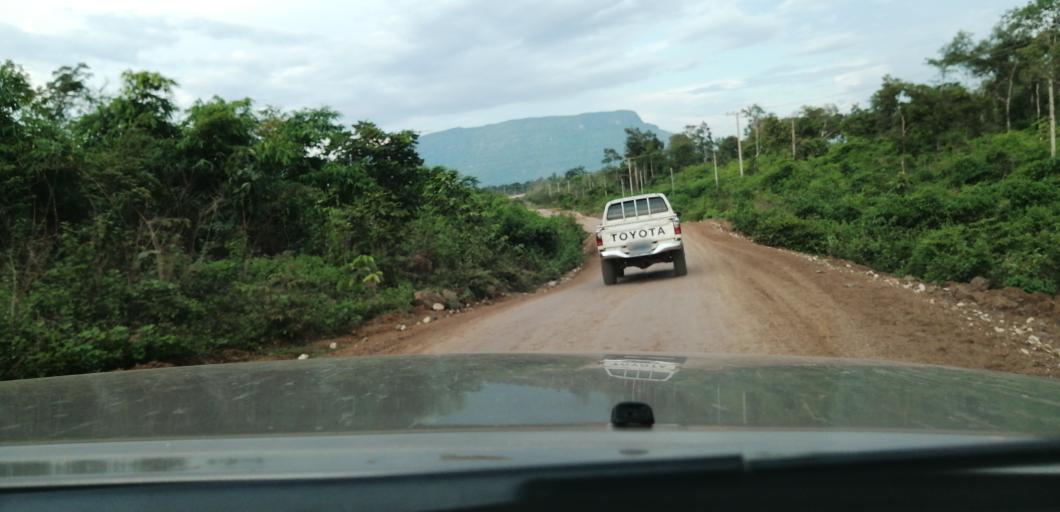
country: LA
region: Attapu
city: Attapu
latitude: 14.7092
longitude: 106.4799
